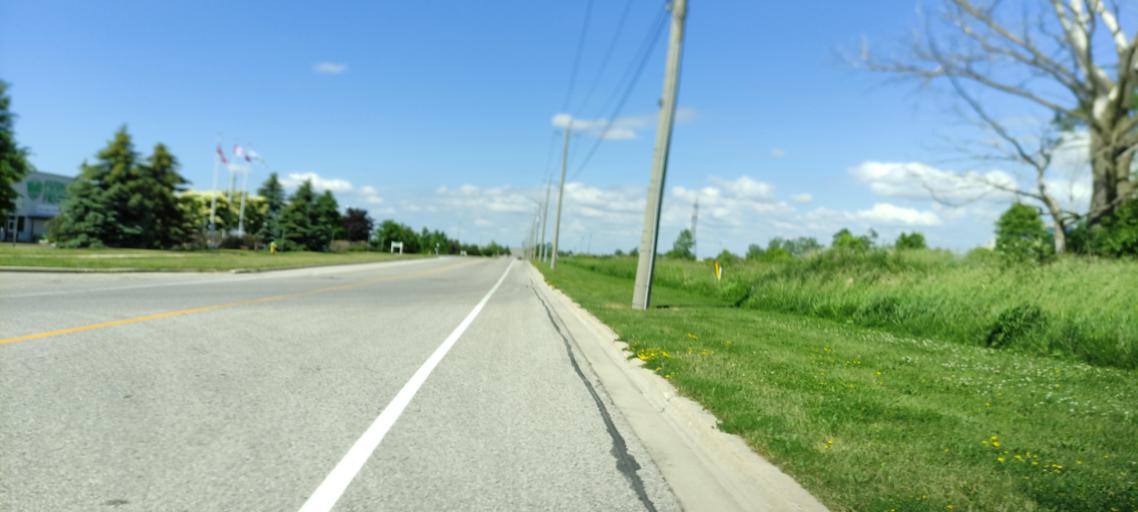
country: CA
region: Ontario
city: Stratford
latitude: 43.3439
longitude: -81.0118
